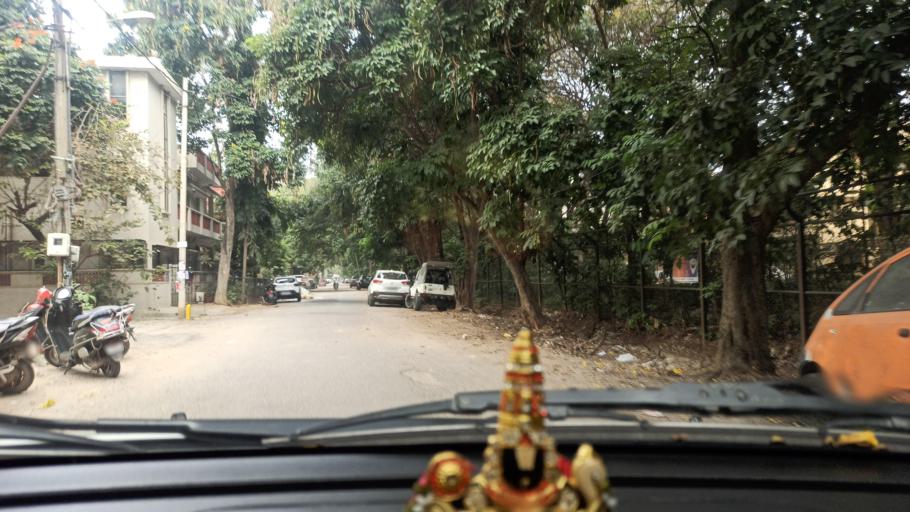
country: IN
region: Karnataka
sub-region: Bangalore Urban
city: Bangalore
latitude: 13.0197
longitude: 77.6449
